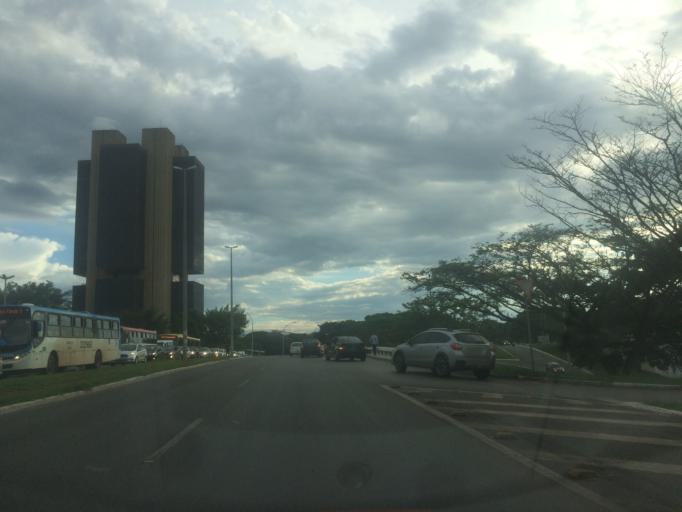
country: BR
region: Federal District
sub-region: Brasilia
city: Brasilia
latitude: -15.8005
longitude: -47.8848
